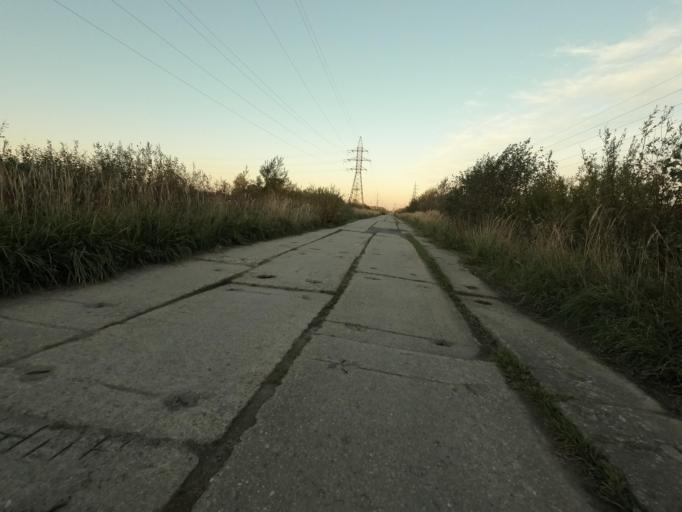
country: RU
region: Leningrad
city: Otradnoye
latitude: 59.7601
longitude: 30.7876
